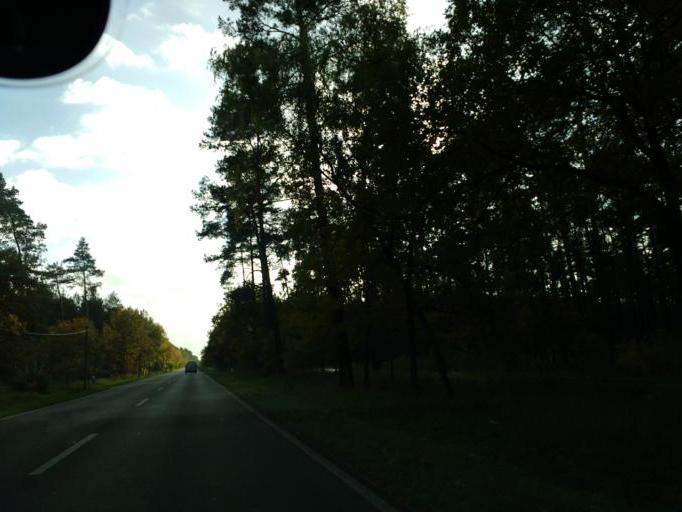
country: DE
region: Brandenburg
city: Grunheide
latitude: 52.4021
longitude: 13.8249
